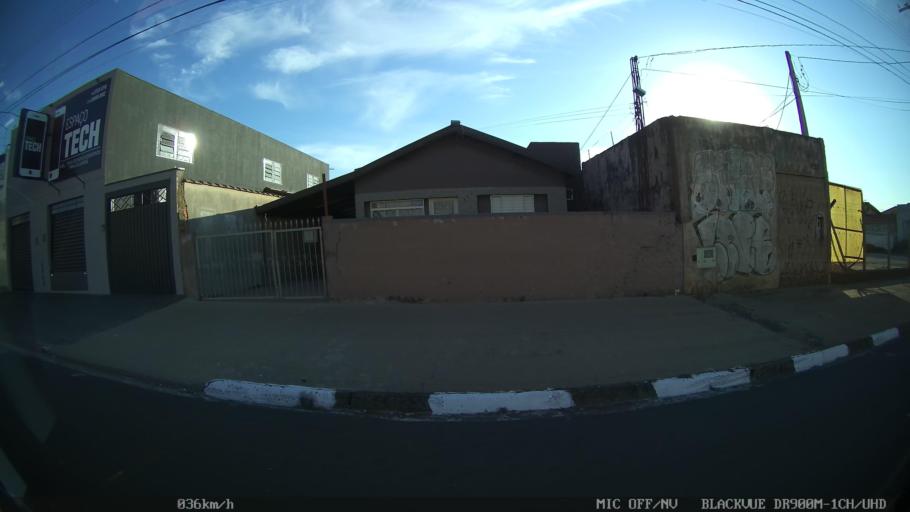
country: BR
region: Sao Paulo
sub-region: Franca
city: Franca
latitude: -20.5247
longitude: -47.3769
